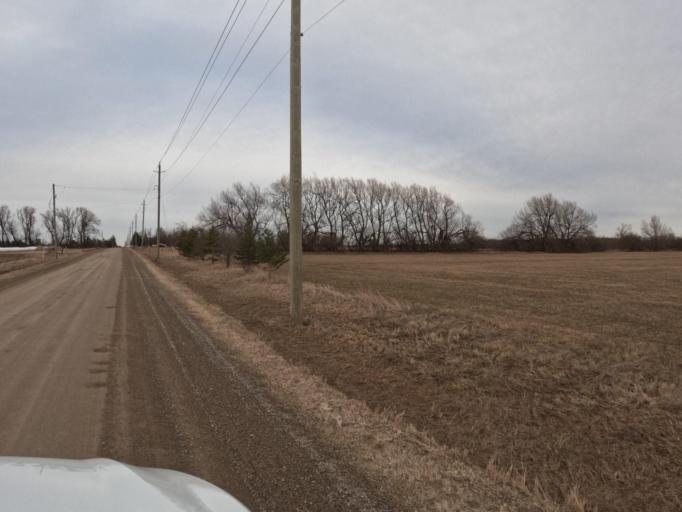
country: CA
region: Ontario
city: Orangeville
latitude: 43.9199
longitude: -80.2245
